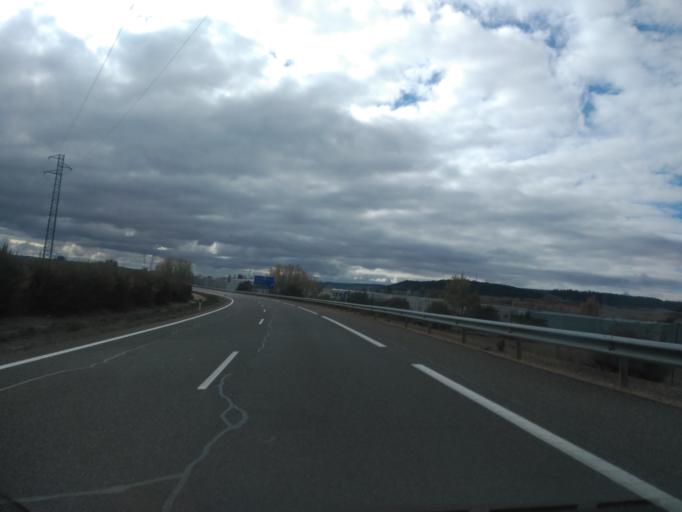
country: ES
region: Castille and Leon
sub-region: Provincia de Palencia
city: Villamuriel de Cerrato
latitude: 41.9685
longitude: -4.5044
